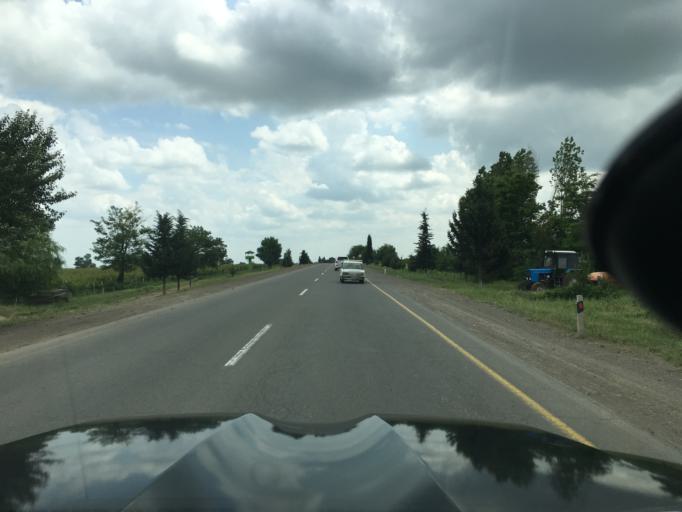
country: AZ
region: Tovuz
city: Tovuz
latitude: 40.9684
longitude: 45.6963
